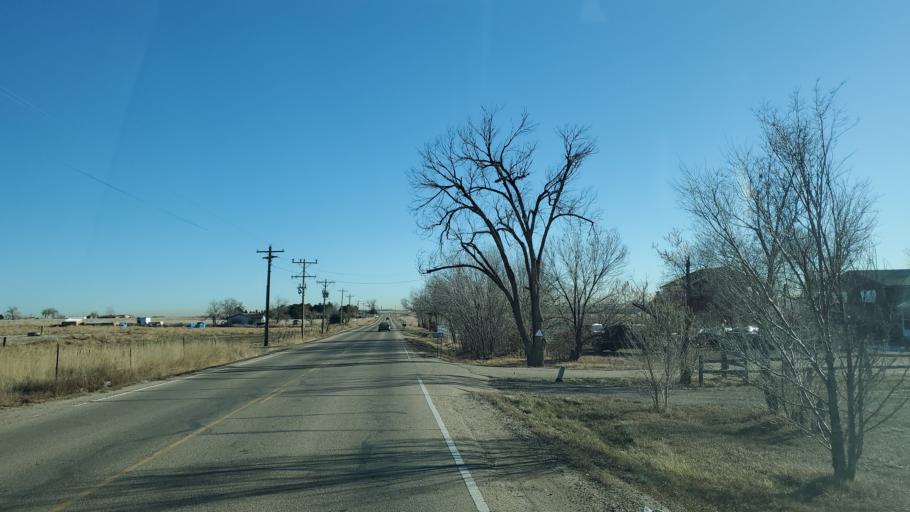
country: US
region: Colorado
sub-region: Boulder County
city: Erie
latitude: 39.9865
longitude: -104.9759
